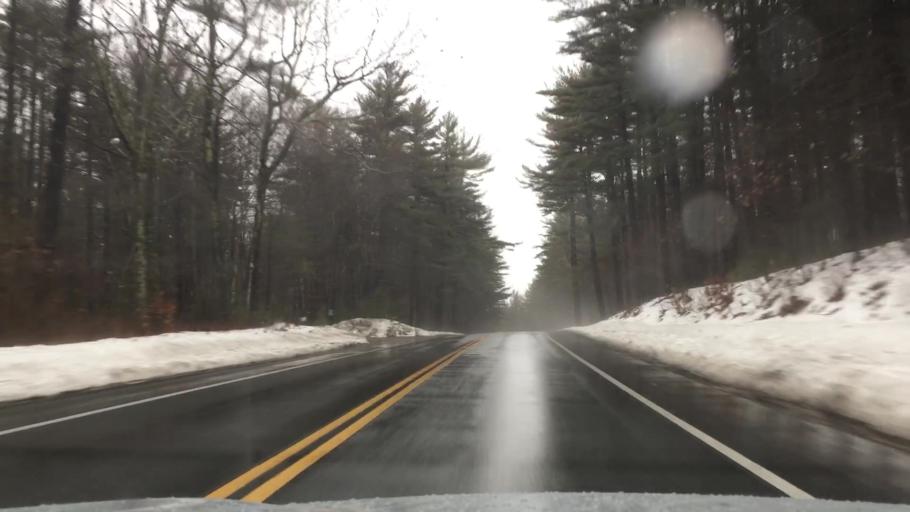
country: US
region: Massachusetts
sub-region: Hampshire County
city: Pelham
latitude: 42.4130
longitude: -72.4016
